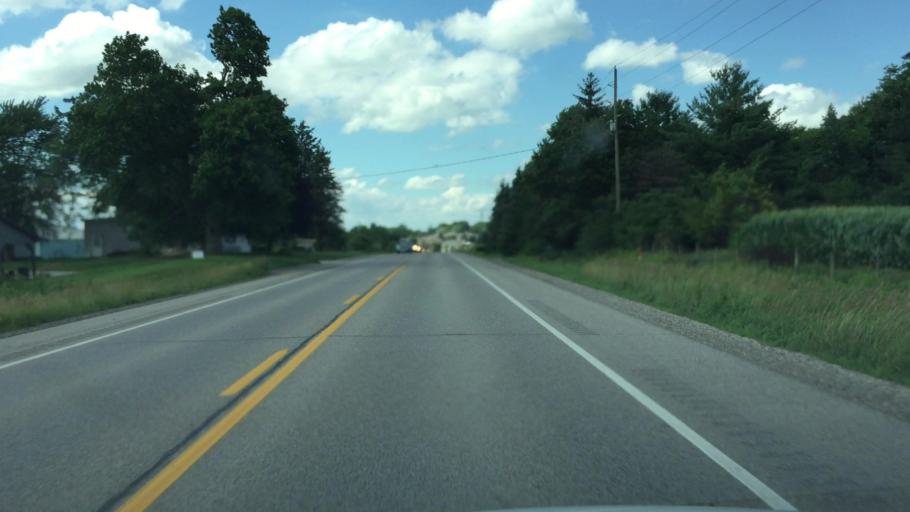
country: US
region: Iowa
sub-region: Johnson County
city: Solon
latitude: 41.7908
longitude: -91.4885
